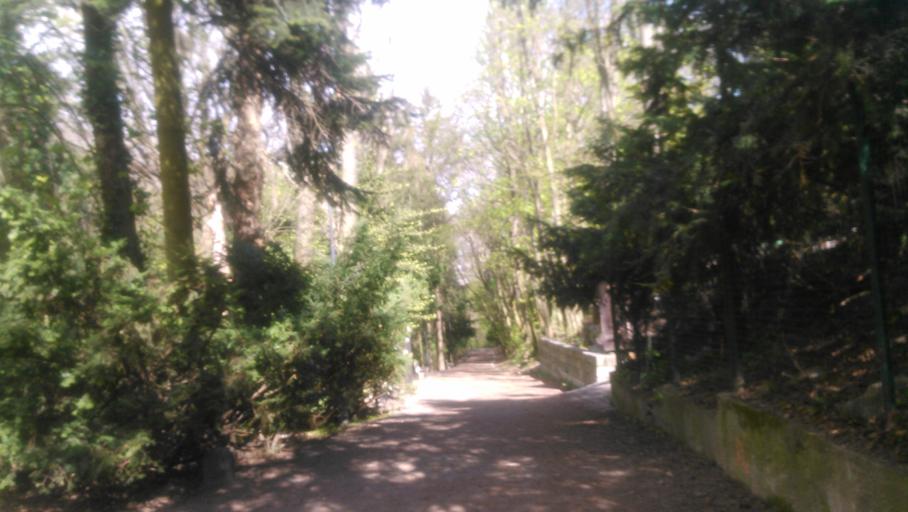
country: SK
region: Bratislavsky
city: Bratislava
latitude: 48.1569
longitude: 17.0947
